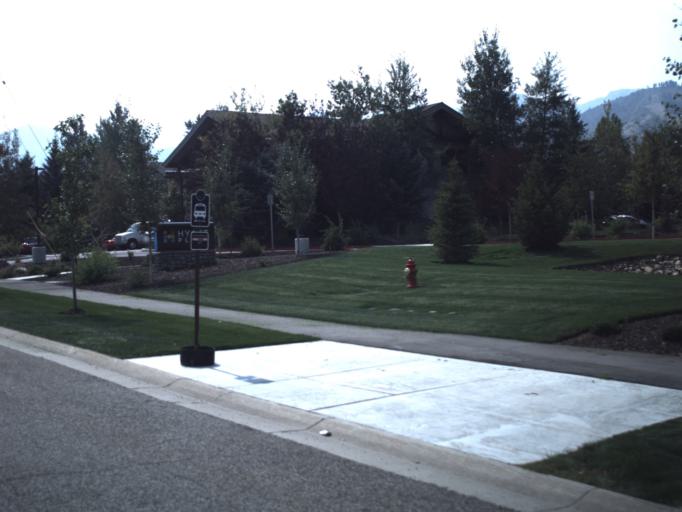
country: US
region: Utah
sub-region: Summit County
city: Snyderville
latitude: 40.6944
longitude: -111.5443
